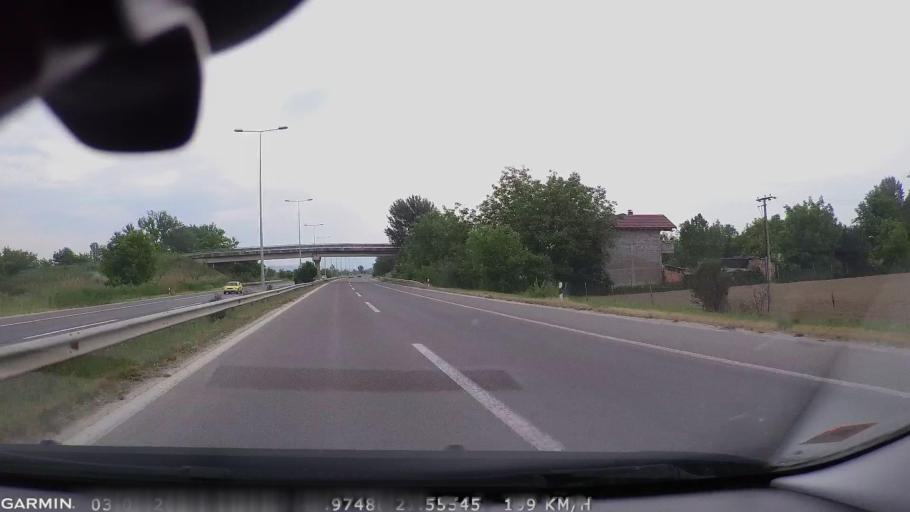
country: MK
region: Ilinden
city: Jurumleri
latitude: 41.9751
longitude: 21.5542
